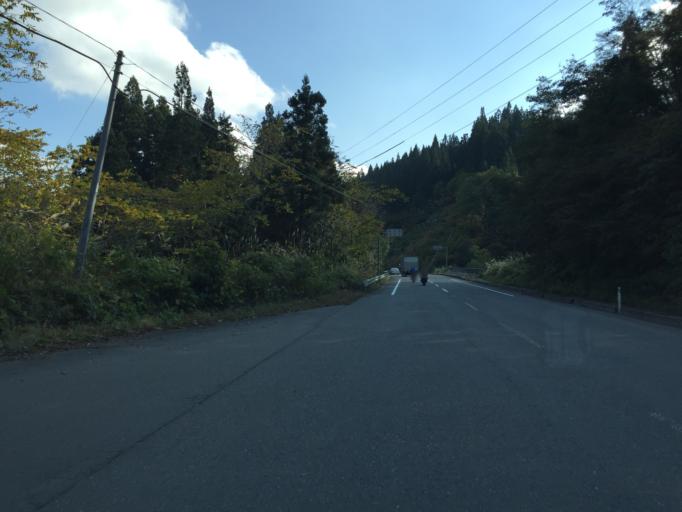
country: JP
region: Yamagata
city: Yonezawa
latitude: 37.8507
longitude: 139.9941
